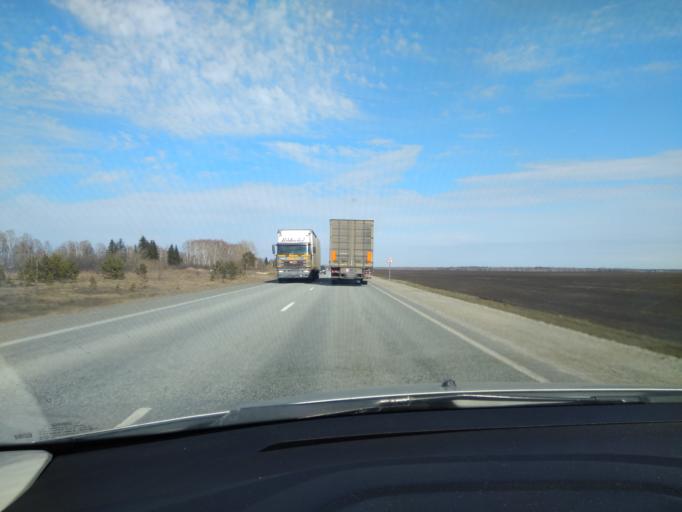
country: RU
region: Sverdlovsk
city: Tugulym
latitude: 57.0704
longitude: 64.6820
